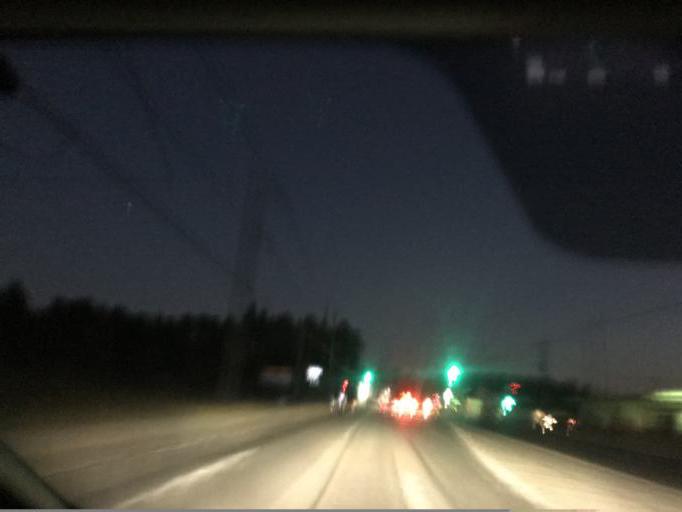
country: JP
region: Ibaraki
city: Ishige
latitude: 36.0909
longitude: 140.0371
